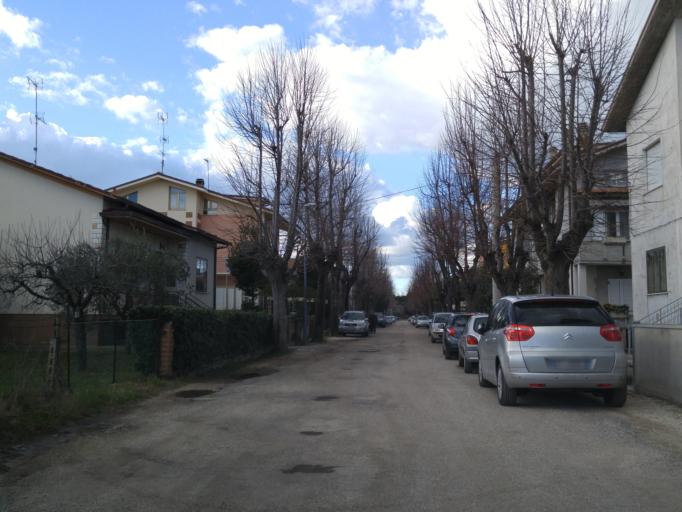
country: IT
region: The Marches
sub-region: Provincia di Pesaro e Urbino
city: Rosciano
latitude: 43.8251
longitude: 13.0026
